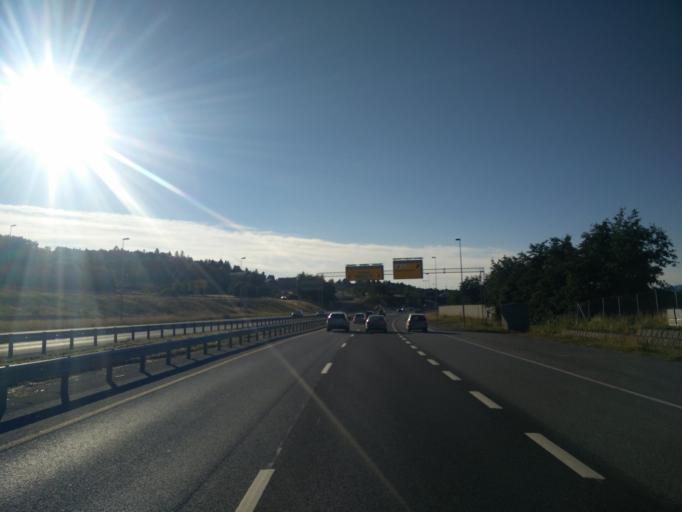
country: NO
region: Sor-Trondelag
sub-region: Trondheim
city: Trondheim
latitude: 63.4231
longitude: 10.5244
